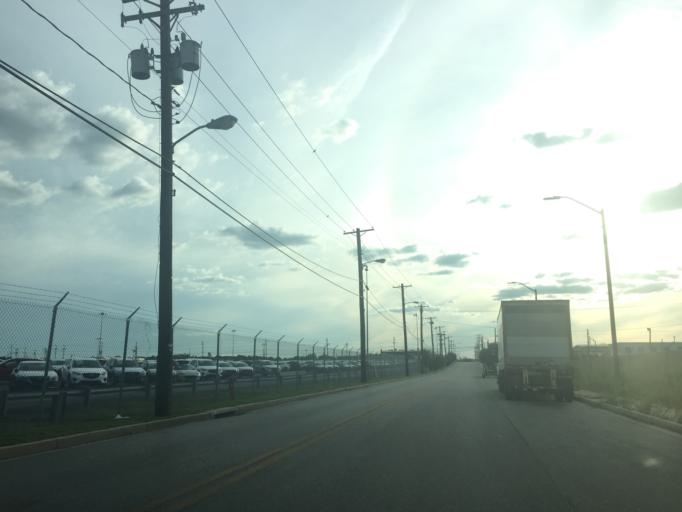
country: US
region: Maryland
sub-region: Anne Arundel County
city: Brooklyn Park
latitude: 39.2378
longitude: -76.5754
